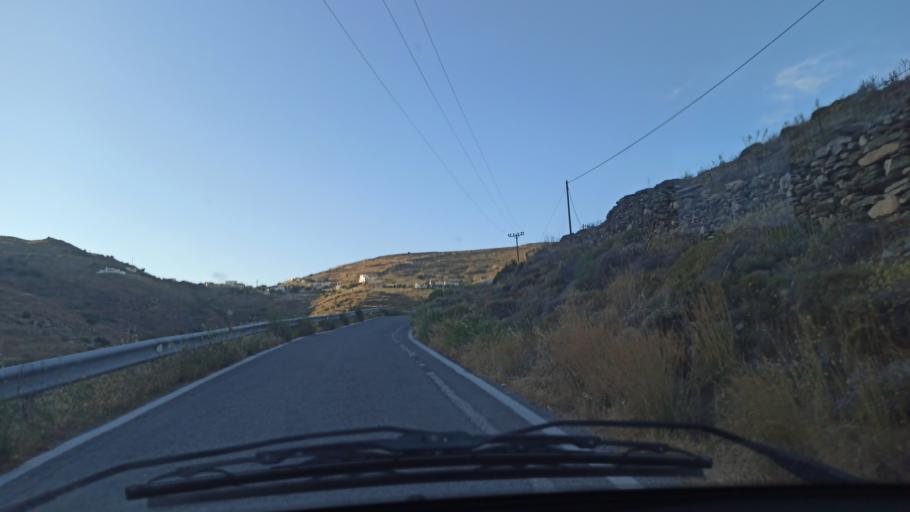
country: GR
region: South Aegean
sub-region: Nomos Kykladon
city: Ano Syros
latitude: 37.4579
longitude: 24.9314
